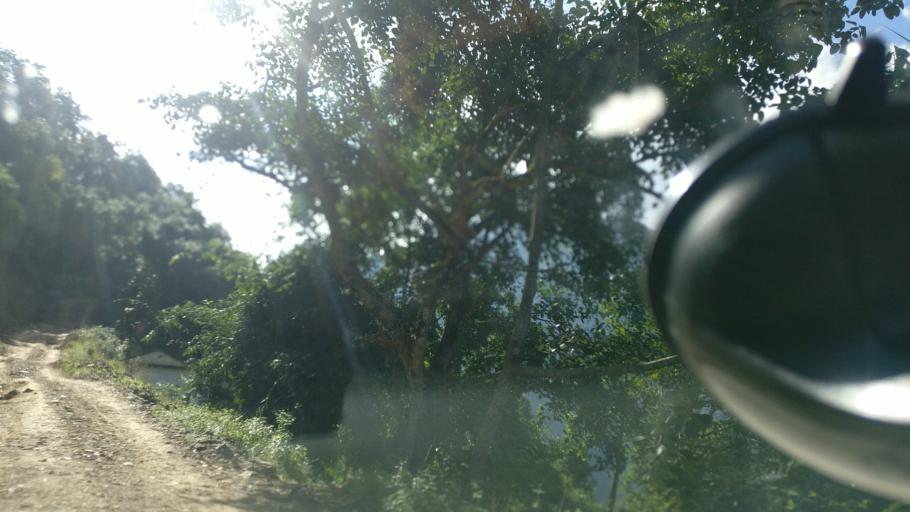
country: NP
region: Western Region
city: Baglung
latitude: 28.1373
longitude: 83.6533
